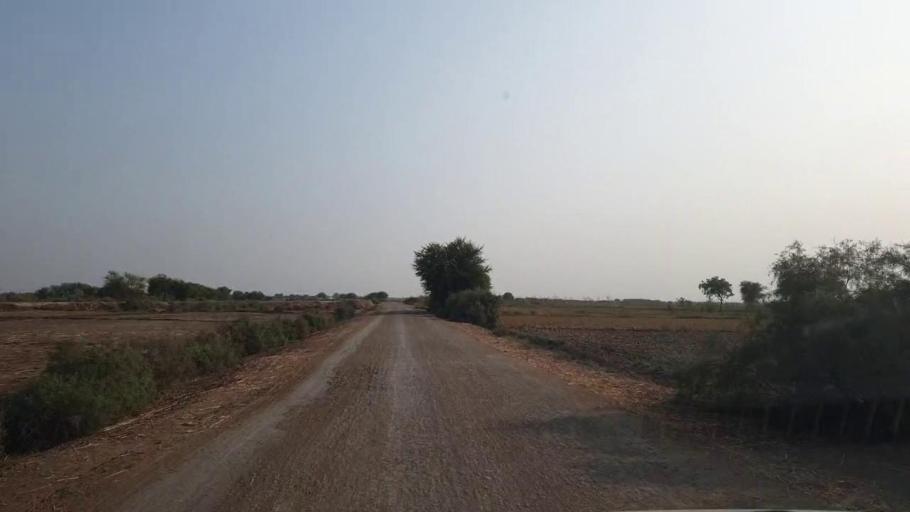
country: PK
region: Sindh
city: Matli
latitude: 25.0556
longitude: 68.7629
